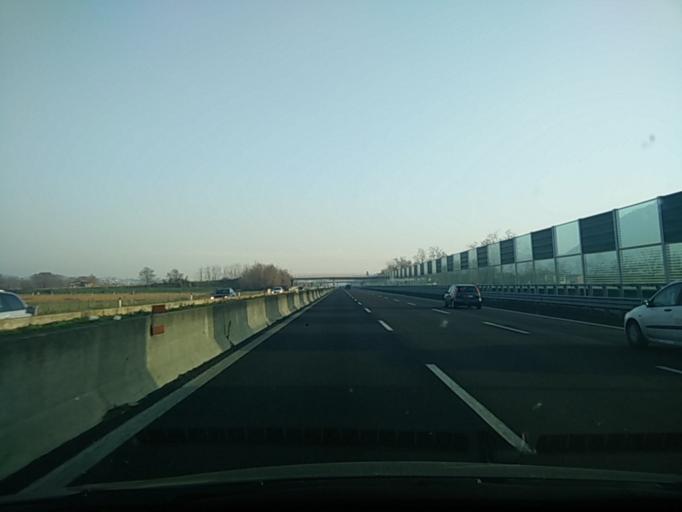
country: IT
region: Lombardy
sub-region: Provincia di Brescia
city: Adro
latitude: 45.6082
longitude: 9.9406
